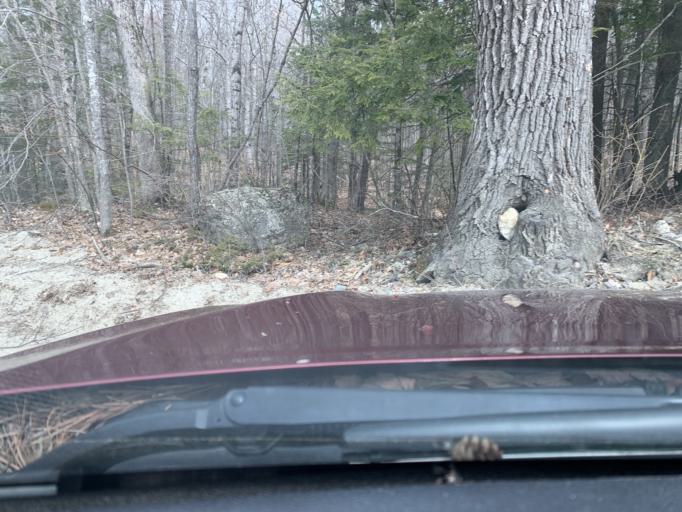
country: US
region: Maine
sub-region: Androscoggin County
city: Poland
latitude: 43.9665
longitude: -70.3825
